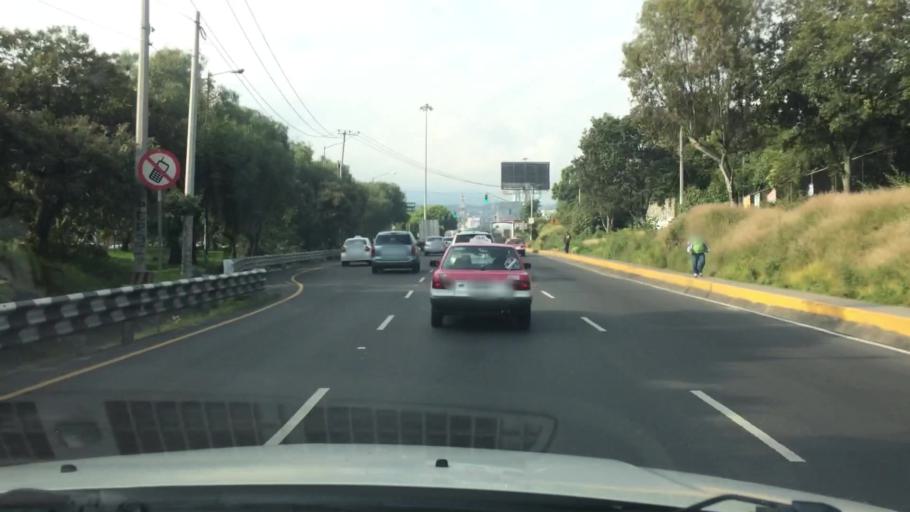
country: MX
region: Mexico City
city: Magdalena Contreras
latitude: 19.2971
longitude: -99.2136
